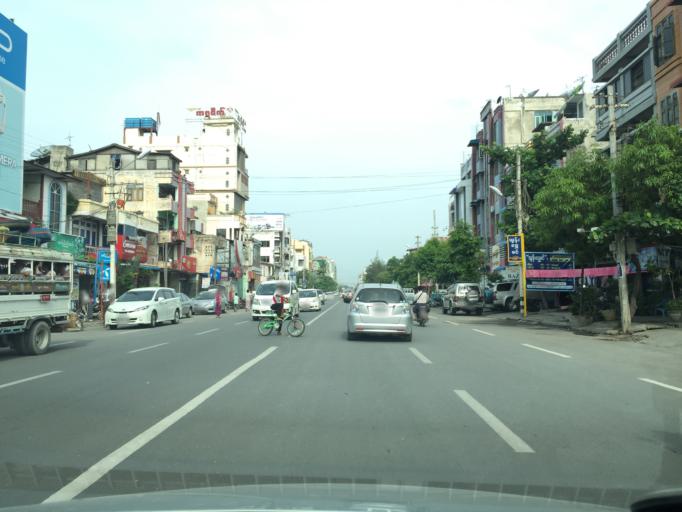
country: MM
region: Mandalay
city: Mandalay
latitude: 21.9688
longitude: 96.0922
